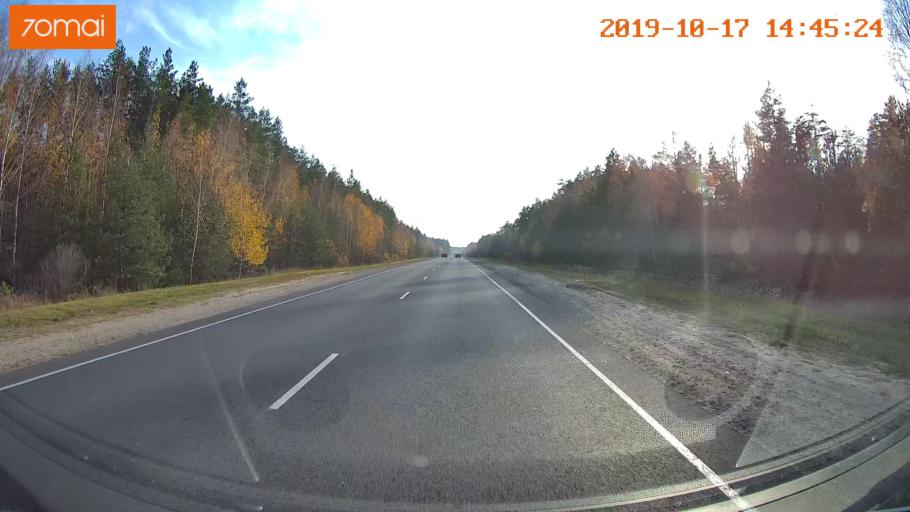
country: RU
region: Rjazan
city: Solotcha
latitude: 54.8015
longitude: 39.8779
